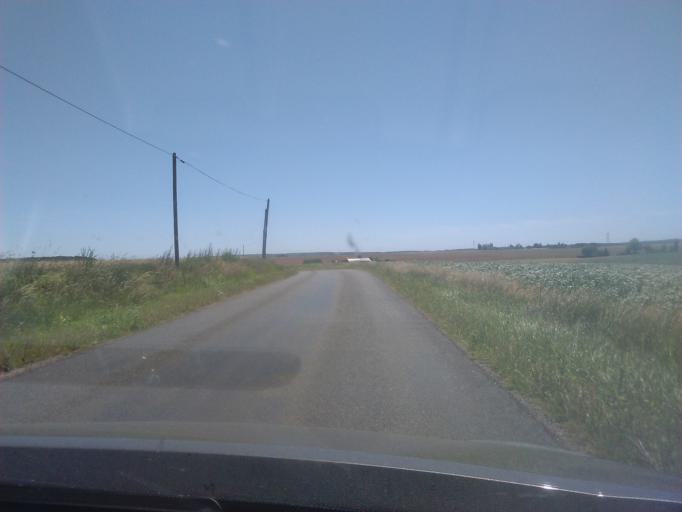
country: FR
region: Centre
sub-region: Departement du Loir-et-Cher
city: Herbault
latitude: 47.6445
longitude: 1.1929
